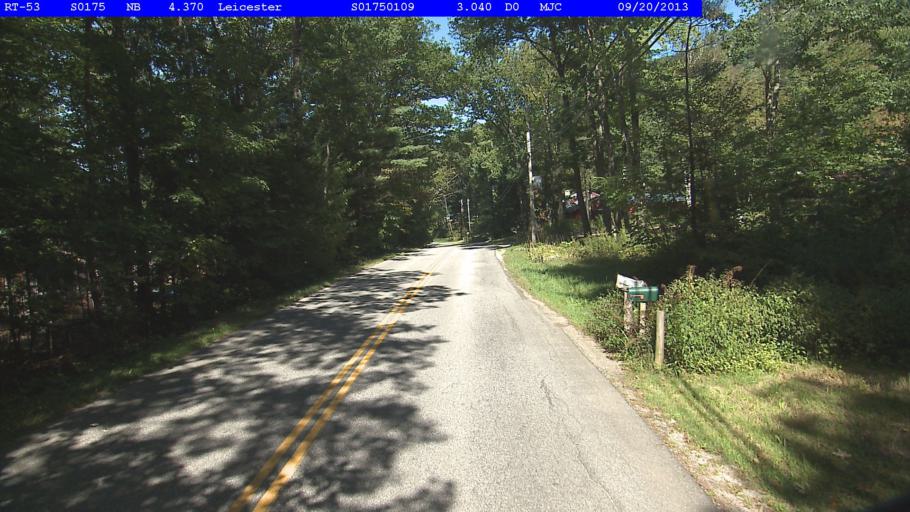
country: US
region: Vermont
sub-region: Rutland County
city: Brandon
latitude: 43.8864
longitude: -73.0644
